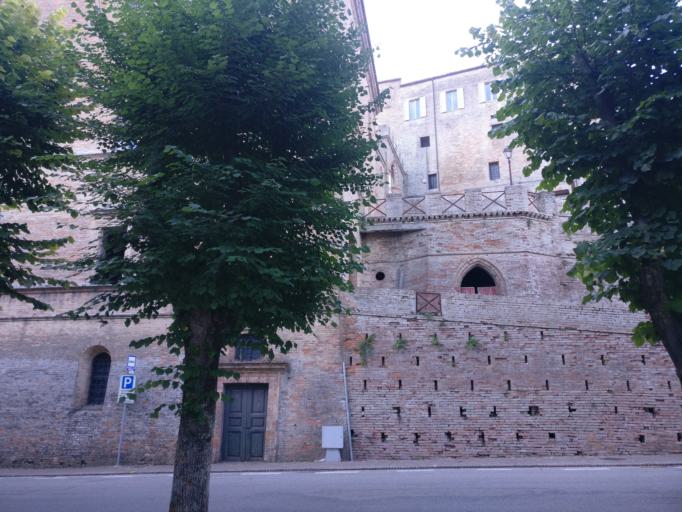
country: IT
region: The Marches
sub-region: Provincia di Ascoli Piceno
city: Montalto delle Marche
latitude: 42.9880
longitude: 13.6067
